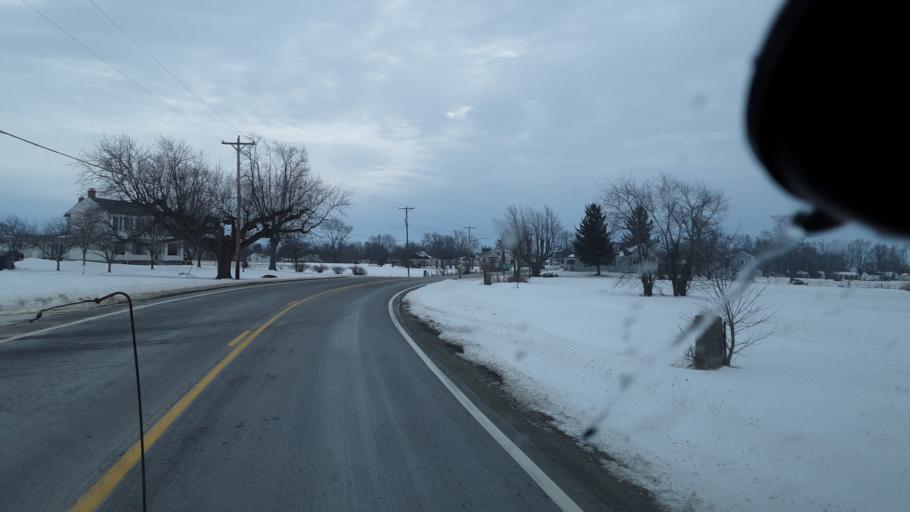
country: US
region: Ohio
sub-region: Madison County
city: Bethel
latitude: 39.7380
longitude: -83.4769
